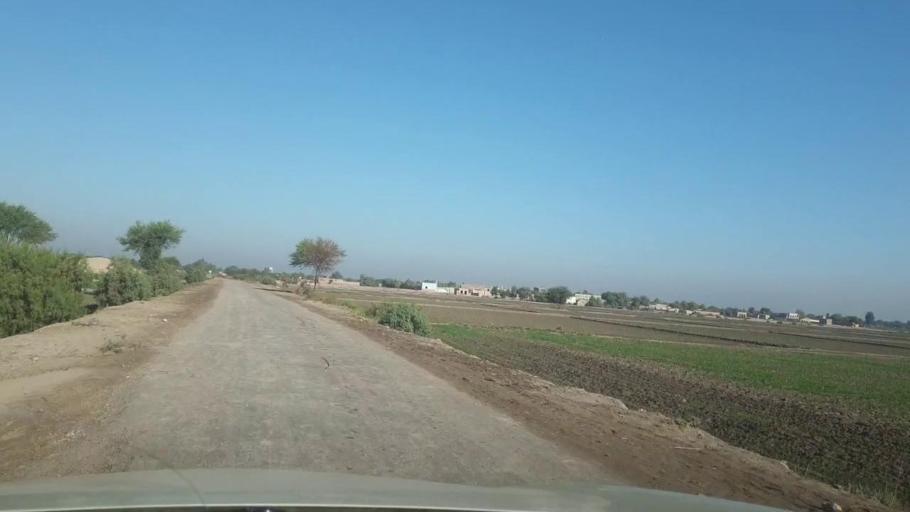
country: PK
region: Sindh
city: Bhan
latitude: 26.5318
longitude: 67.6746
